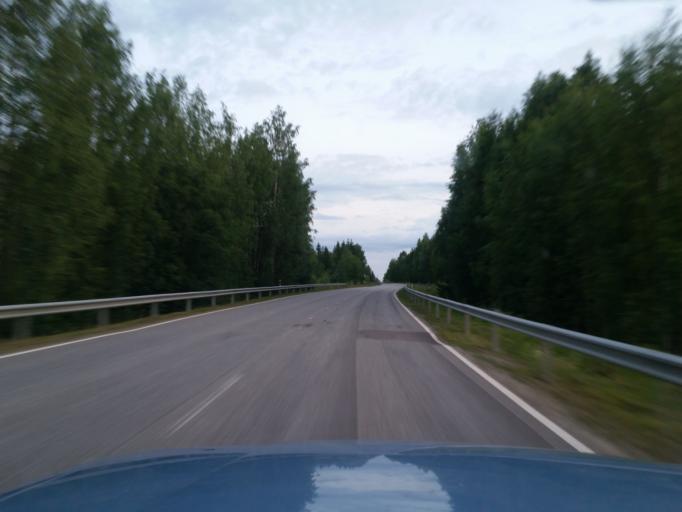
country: FI
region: Southern Savonia
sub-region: Savonlinna
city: Sulkava
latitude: 61.8223
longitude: 28.4393
